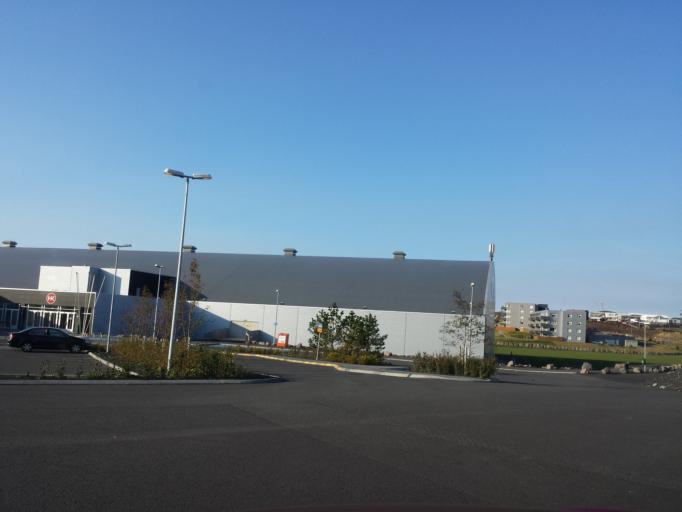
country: IS
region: Capital Region
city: Reykjavik
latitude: 64.0831
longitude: -21.8225
